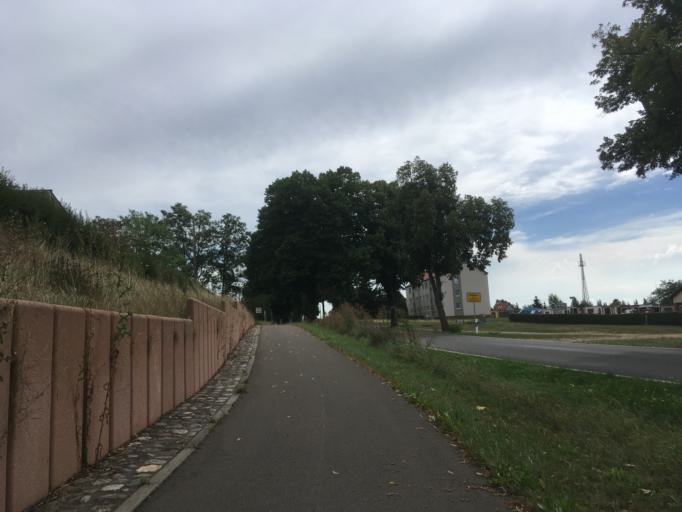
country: DE
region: Brandenburg
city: Mittenwalde
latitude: 53.2193
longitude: 13.6810
